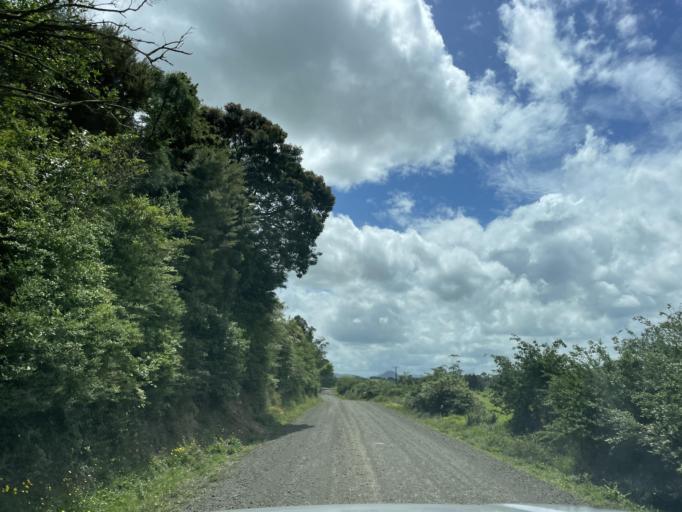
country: NZ
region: Northland
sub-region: Kaipara District
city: Dargaville
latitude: -35.8769
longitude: 174.0381
